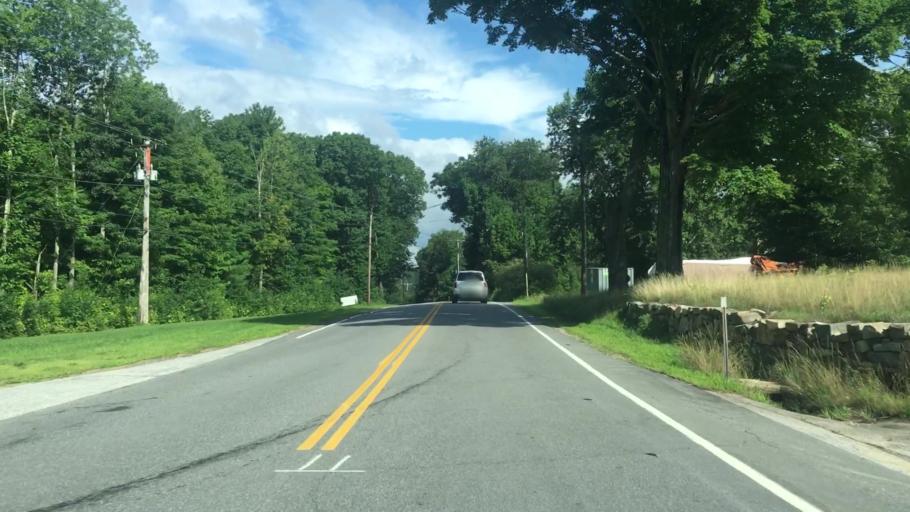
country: US
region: New Hampshire
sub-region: Belknap County
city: Gilford
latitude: 43.5507
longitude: -71.3590
